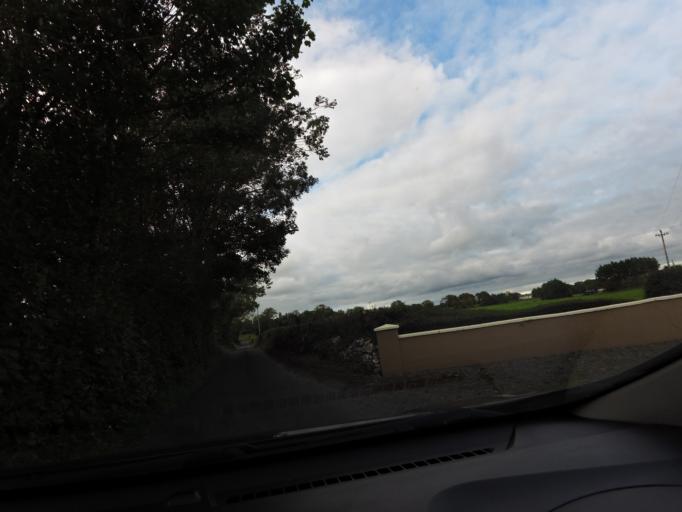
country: IE
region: Connaught
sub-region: County Galway
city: Ballinasloe
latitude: 53.3103
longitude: -8.1020
